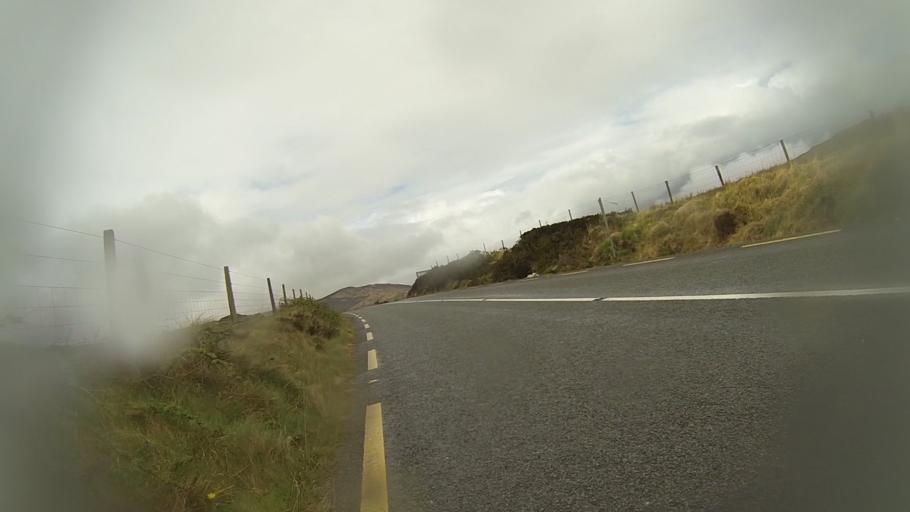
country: IE
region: Munster
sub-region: Ciarrai
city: Kenmare
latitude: 51.8010
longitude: -9.5720
